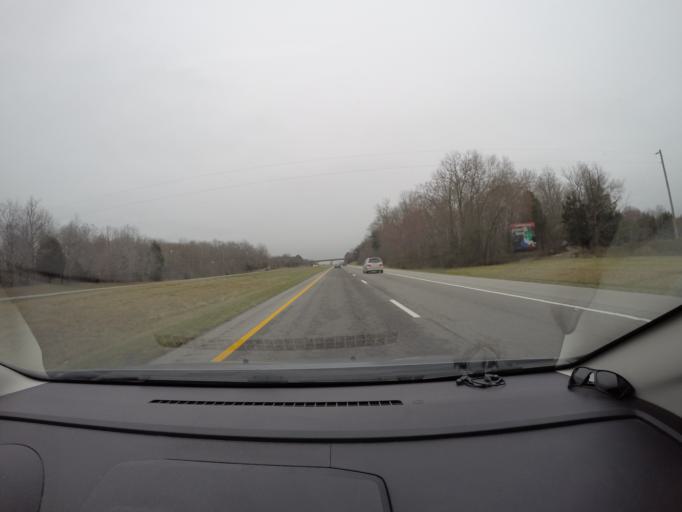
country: US
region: Tennessee
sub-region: Coffee County
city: Manchester
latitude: 35.4005
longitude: -85.9994
